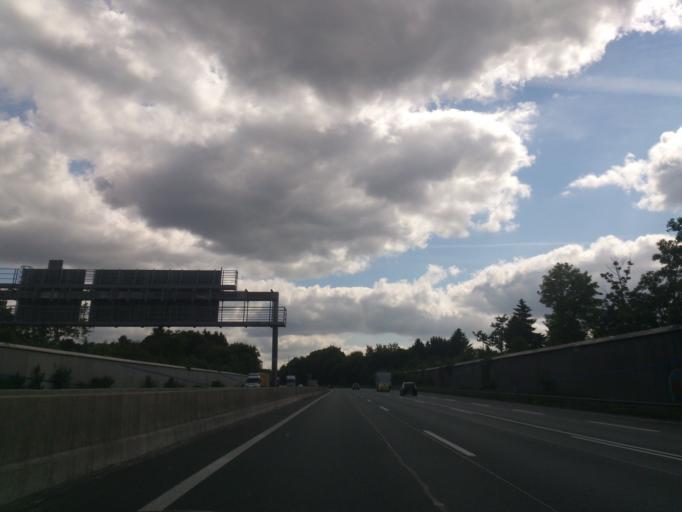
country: DE
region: North Rhine-Westphalia
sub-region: Regierungsbezirk Detmold
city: Oerlinghausen
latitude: 51.9899
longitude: 8.6160
